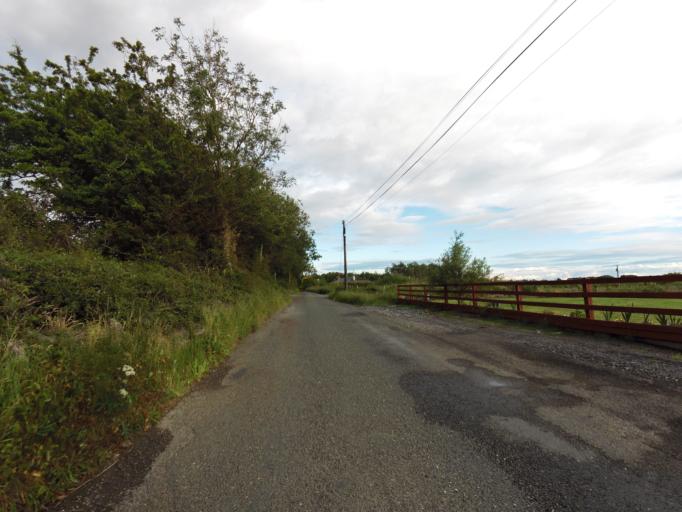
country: IE
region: Connaught
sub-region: County Galway
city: Athenry
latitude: 53.2956
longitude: -8.7328
